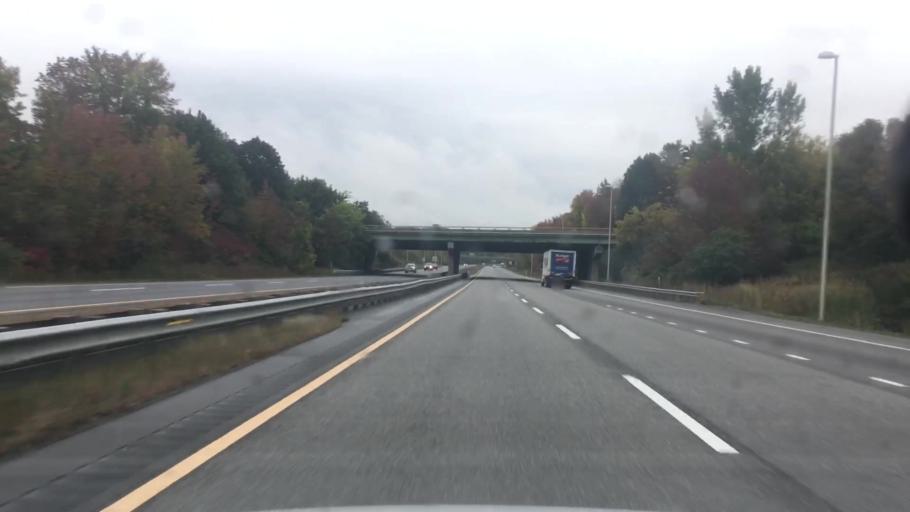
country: US
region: Maine
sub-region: Kennebec County
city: Augusta
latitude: 44.3153
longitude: -69.8110
